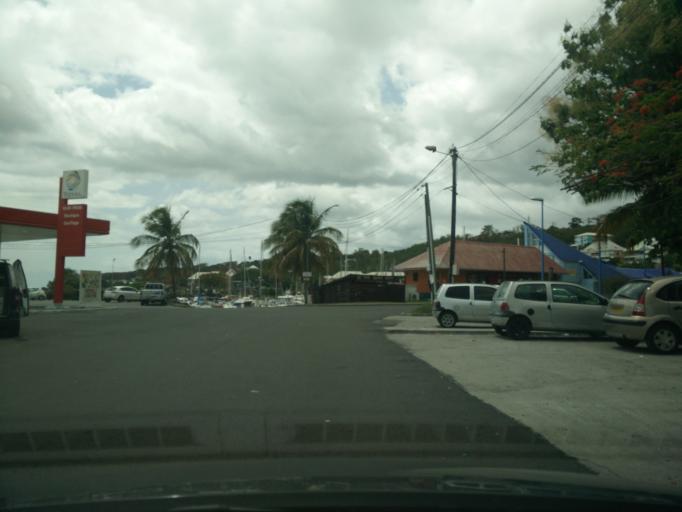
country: GP
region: Guadeloupe
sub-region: Guadeloupe
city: Basse-Terre
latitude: 15.9812
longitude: -61.7154
